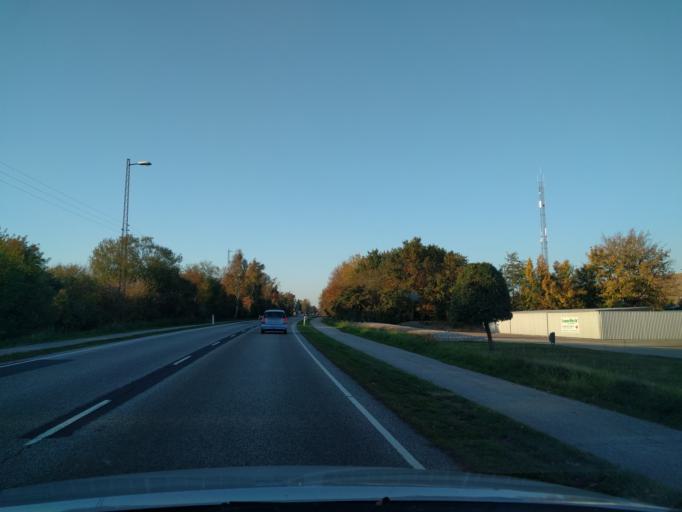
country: DK
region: Zealand
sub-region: Guldborgsund Kommune
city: Nykobing Falster
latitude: 54.7567
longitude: 11.8944
